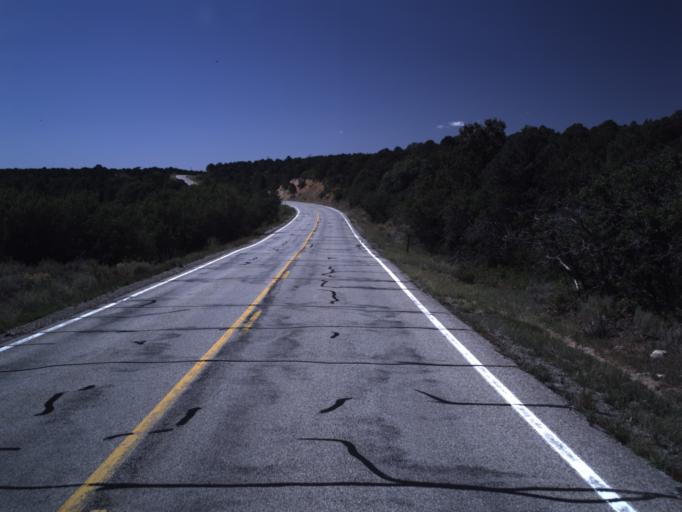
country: US
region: Utah
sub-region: Grand County
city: Moab
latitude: 38.3346
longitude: -109.2145
